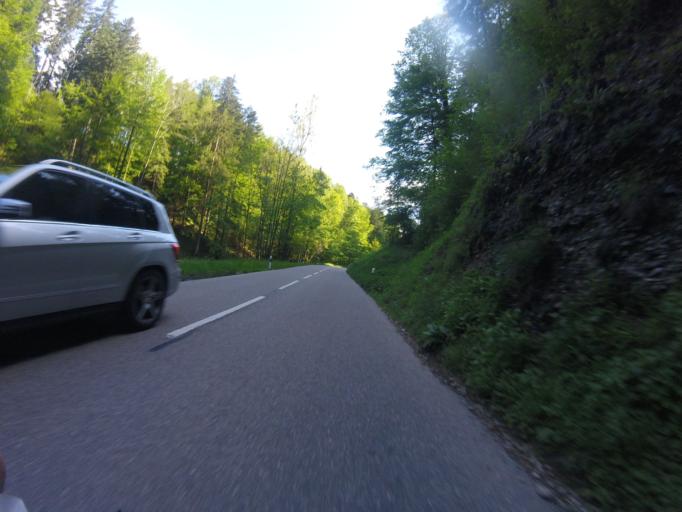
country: CH
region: Saint Gallen
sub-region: Wahlkreis Toggenburg
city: Mogelsberg
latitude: 47.3633
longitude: 9.1586
